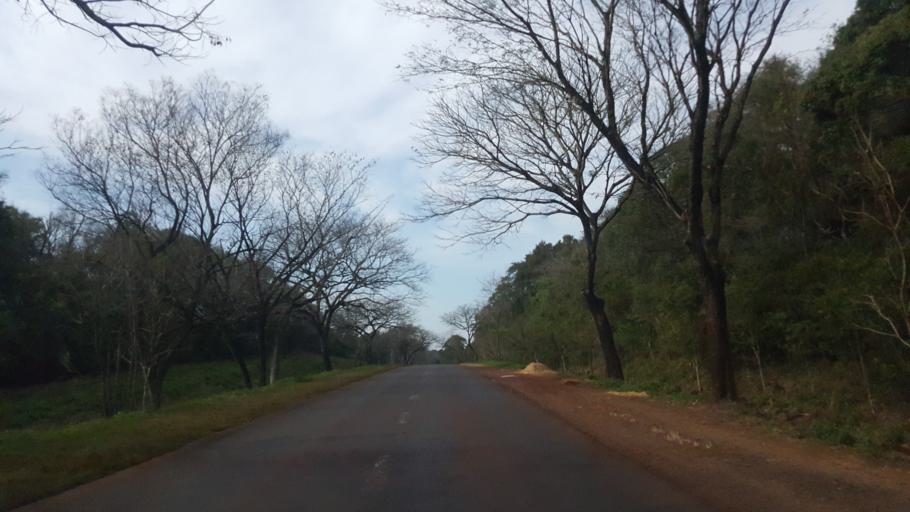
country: AR
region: Misiones
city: Capiovi
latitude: -26.9361
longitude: -55.0830
